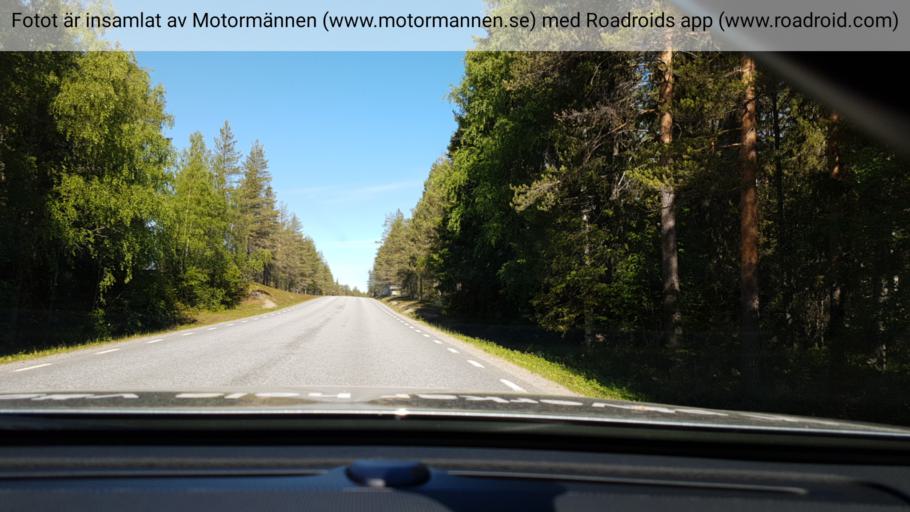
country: SE
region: Vaesterbotten
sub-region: Bjurholms Kommun
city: Bjurholm
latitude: 63.9710
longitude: 18.8320
